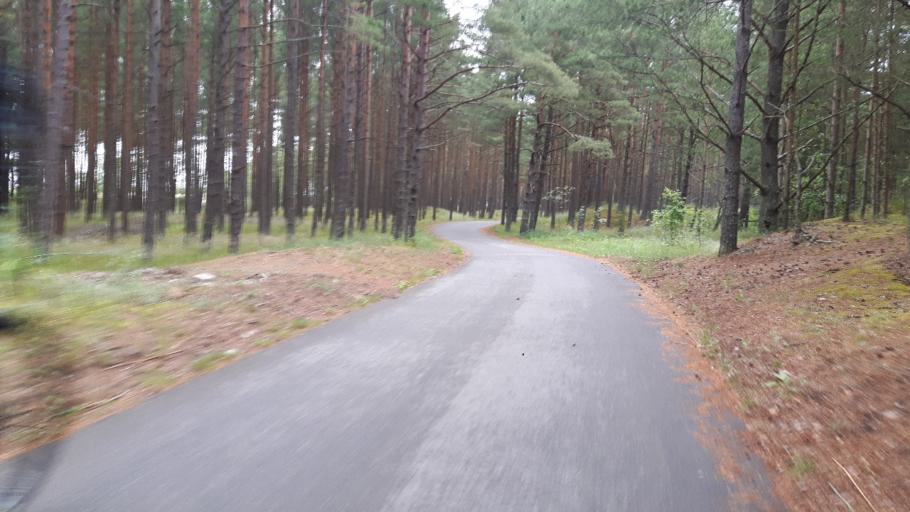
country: LT
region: Klaipedos apskritis
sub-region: Palanga
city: Sventoji
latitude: 55.9839
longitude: 21.0739
